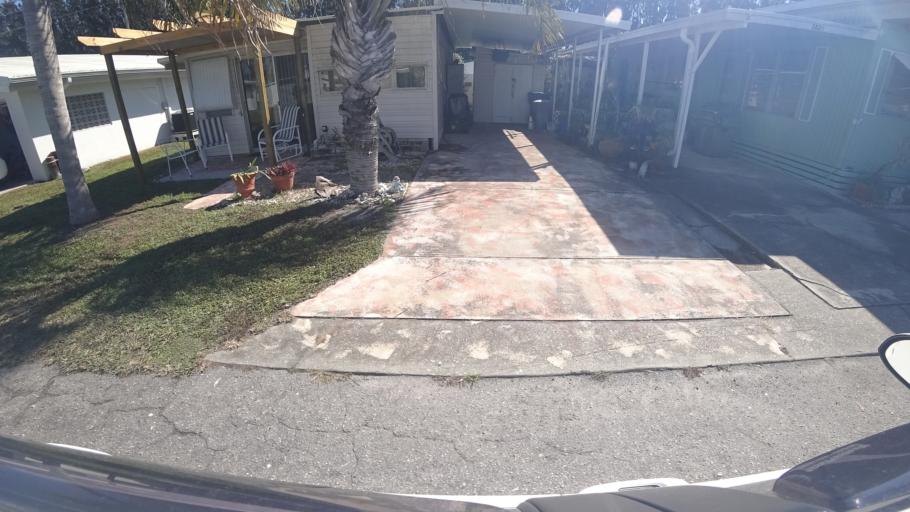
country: US
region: Florida
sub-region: Manatee County
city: Cortez
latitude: 27.4716
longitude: -82.6754
